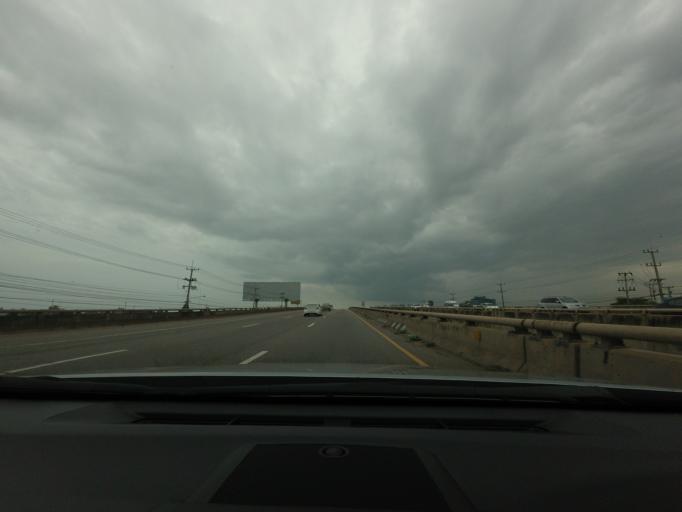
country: TH
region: Samut Sakhon
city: Ban Phaeo
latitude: 13.4875
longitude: 100.1214
